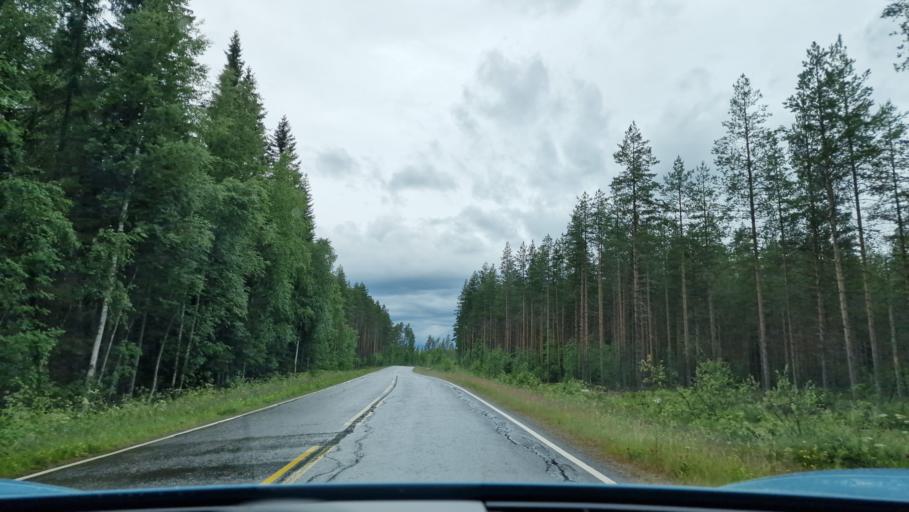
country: FI
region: Central Finland
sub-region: Saarijaervi-Viitasaari
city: Pylkoenmaeki
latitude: 62.6694
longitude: 24.5231
